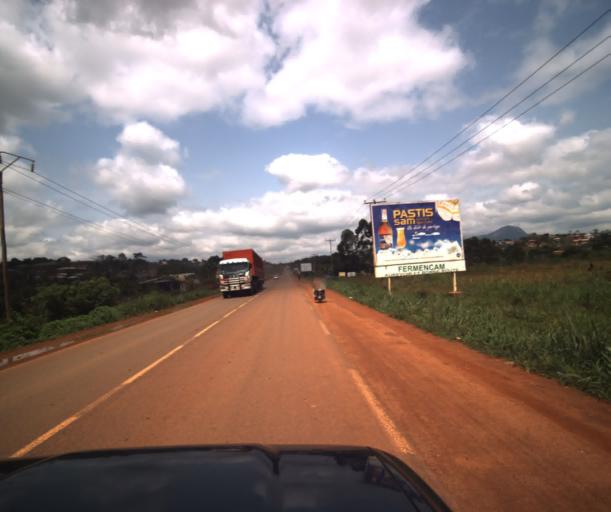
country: CM
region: Centre
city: Yaounde
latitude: 3.7946
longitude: 11.4851
